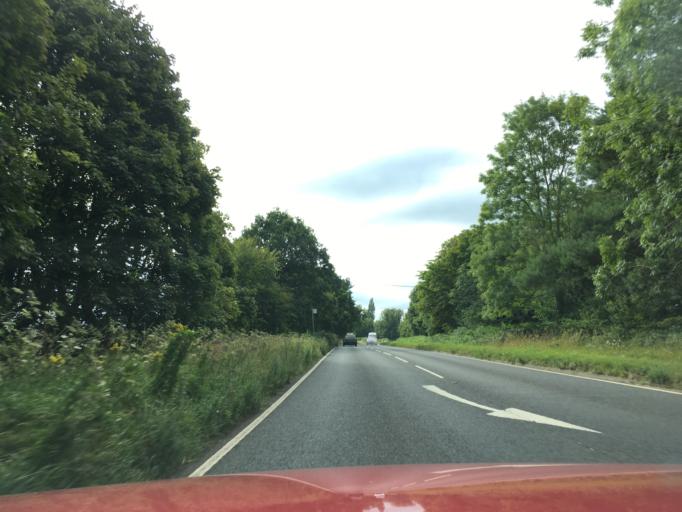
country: GB
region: England
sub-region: West Sussex
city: Milland
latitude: 51.0071
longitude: -0.8358
